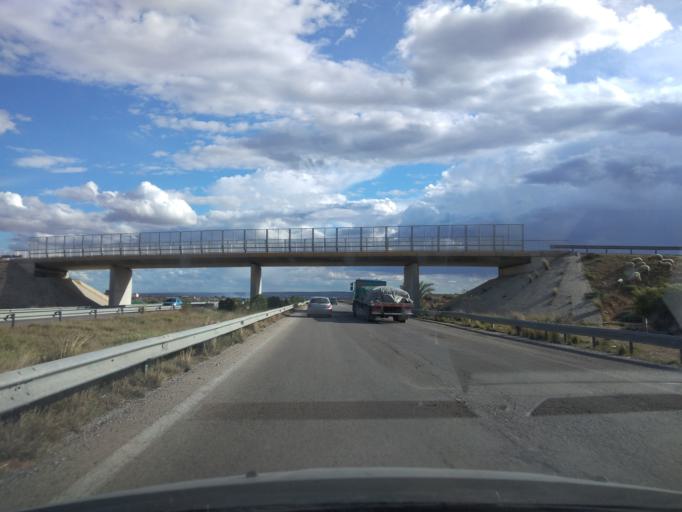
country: TN
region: Al Munastir
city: Manzil Kamil
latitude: 35.5401
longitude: 10.6228
